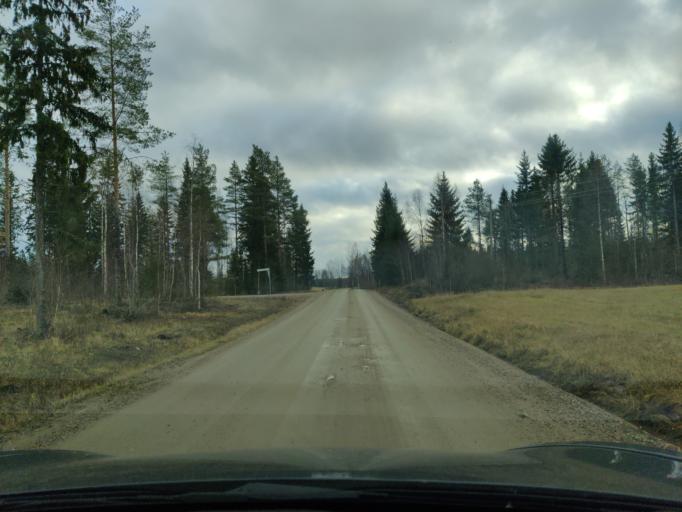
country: FI
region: Northern Savo
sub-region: Ylae-Savo
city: Kiuruvesi
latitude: 63.6383
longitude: 26.6457
